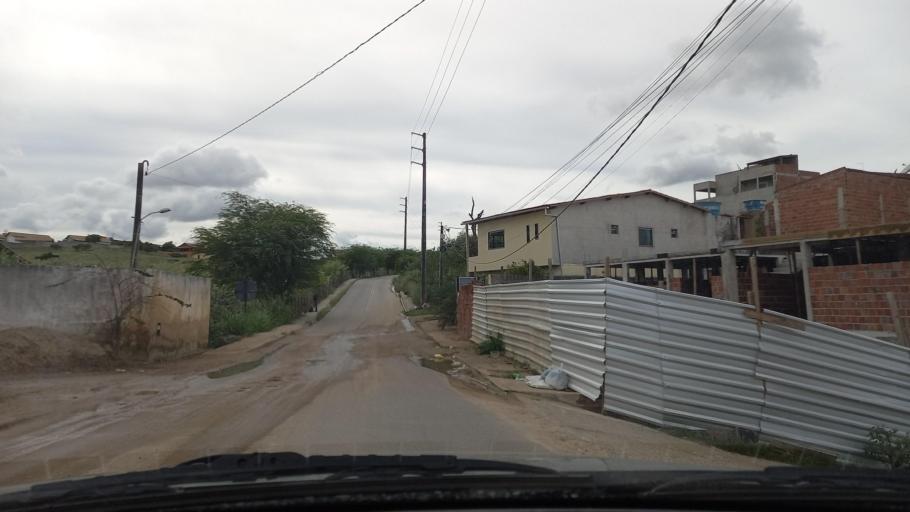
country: BR
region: Pernambuco
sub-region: Gravata
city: Gravata
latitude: -8.2168
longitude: -35.5784
